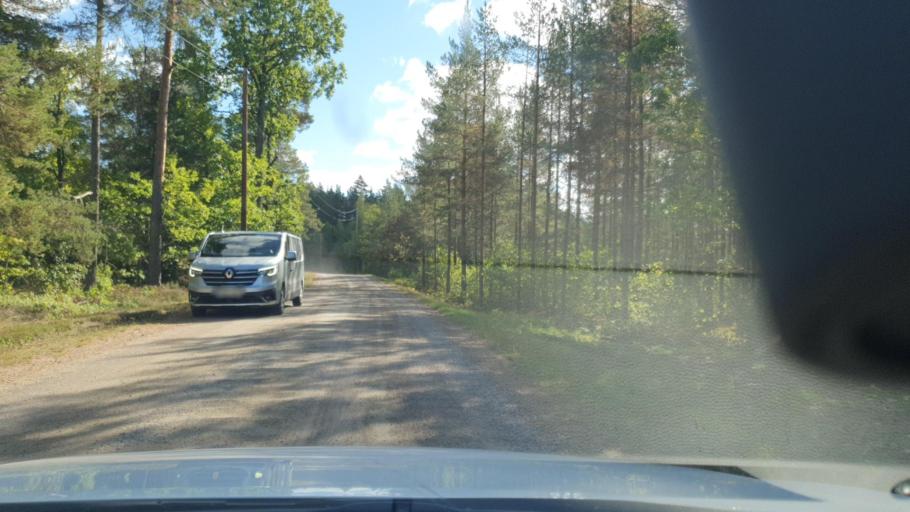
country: SE
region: Kalmar
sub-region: Vasterviks Kommun
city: Ankarsrum
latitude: 57.6983
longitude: 16.4580
